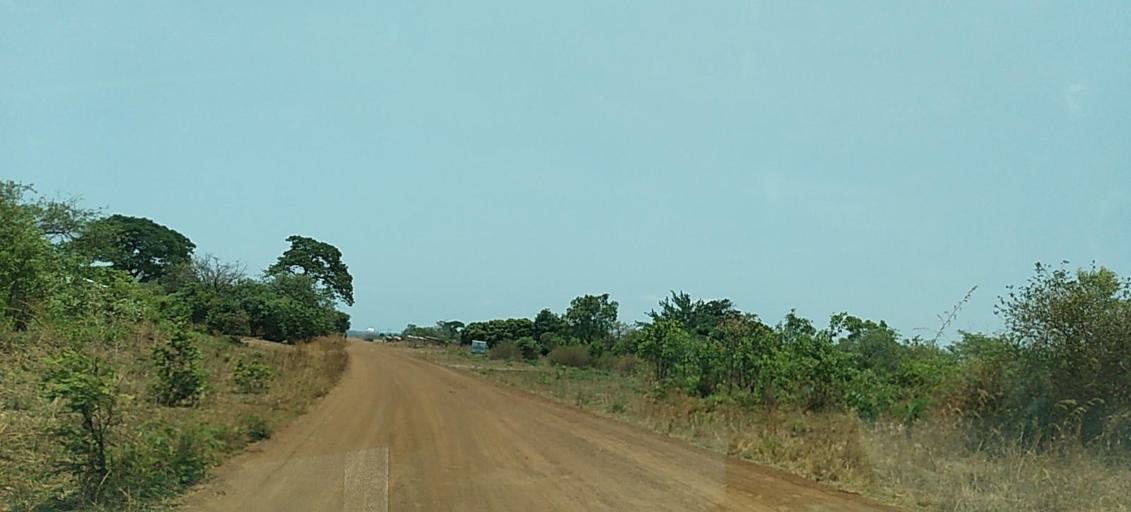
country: ZM
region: Copperbelt
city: Mpongwe
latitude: -13.6762
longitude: 27.8564
